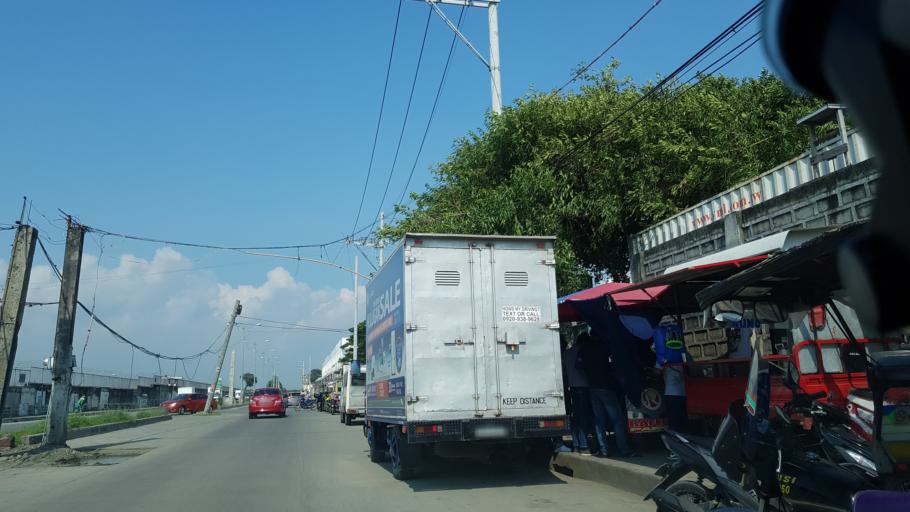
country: PH
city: Sambayanihan People's Village
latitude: 14.5001
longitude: 121.0076
